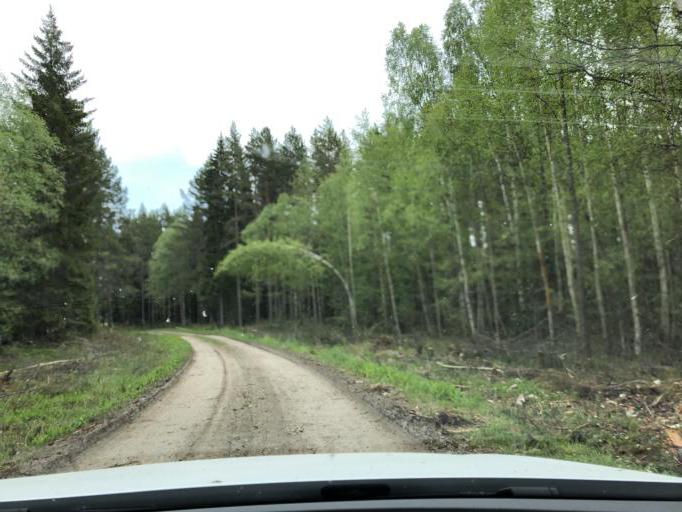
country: SE
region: Uppsala
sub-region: Heby Kommun
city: OEstervala
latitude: 60.3740
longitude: 17.2327
